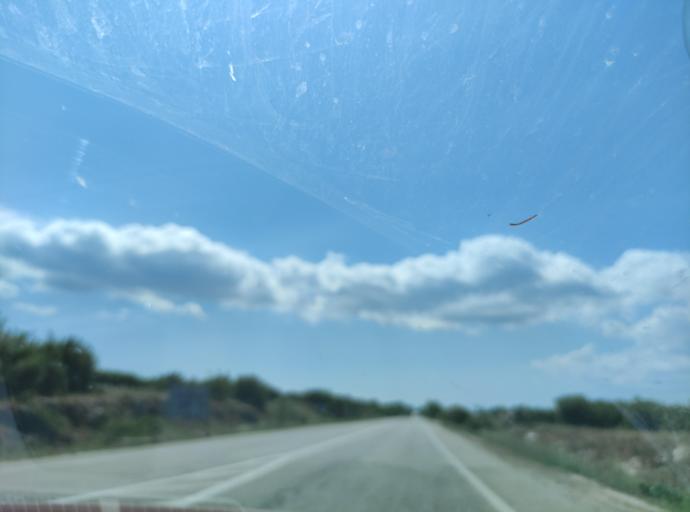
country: GR
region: East Macedonia and Thrace
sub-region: Nomos Dramas
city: Fotolivos
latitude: 40.9913
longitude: 24.0726
